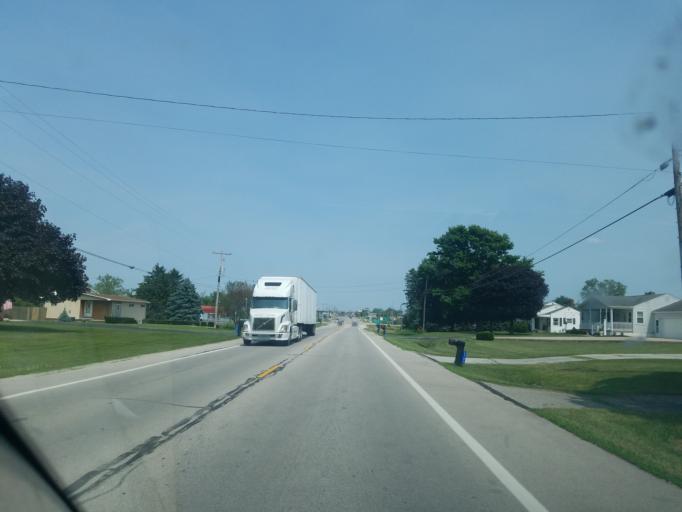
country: US
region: Ohio
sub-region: Seneca County
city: Tiffin
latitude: 41.1083
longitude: -83.2244
